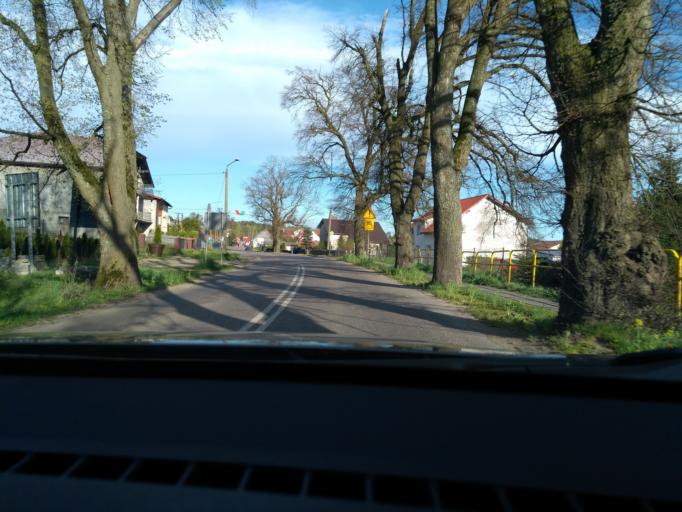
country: PL
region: Pomeranian Voivodeship
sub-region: Powiat kartuski
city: Suleczyno
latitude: 54.3258
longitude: 17.7910
